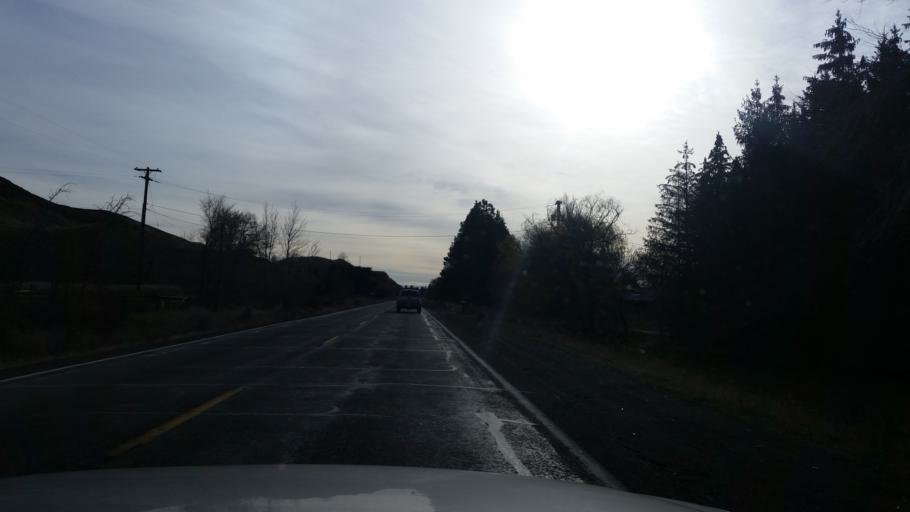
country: US
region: Washington
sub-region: Kittitas County
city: Ellensburg
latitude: 47.0856
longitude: -120.6774
